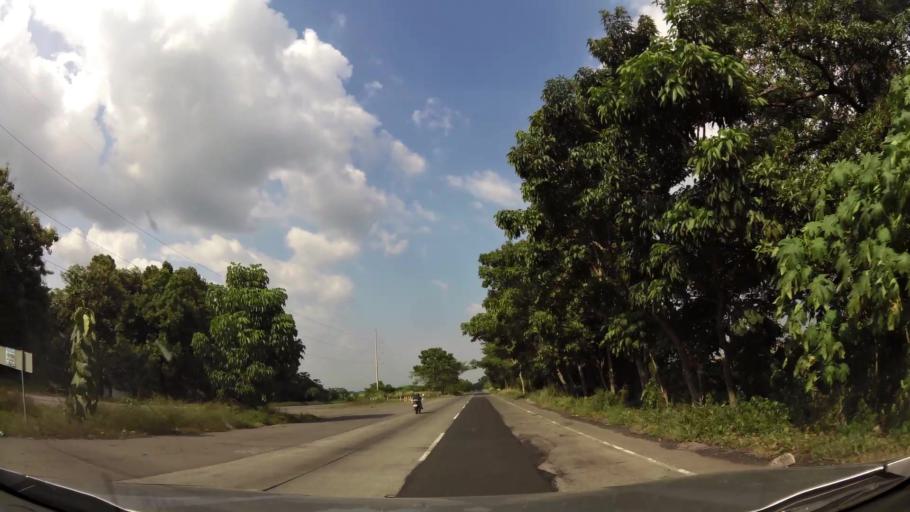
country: GT
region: Escuintla
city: Puerto San Jose
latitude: 14.0444
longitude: -90.7779
